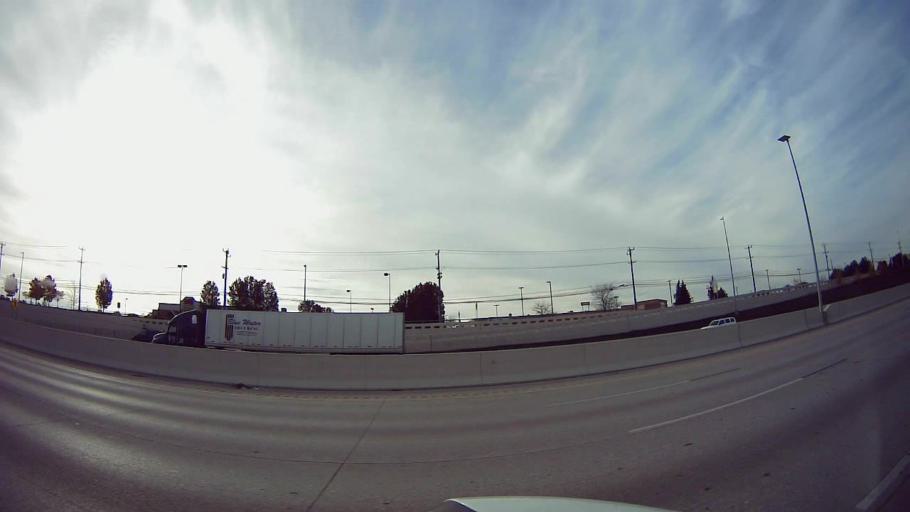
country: US
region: Michigan
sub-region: Wayne County
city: Livonia
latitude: 42.3837
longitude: -83.3306
